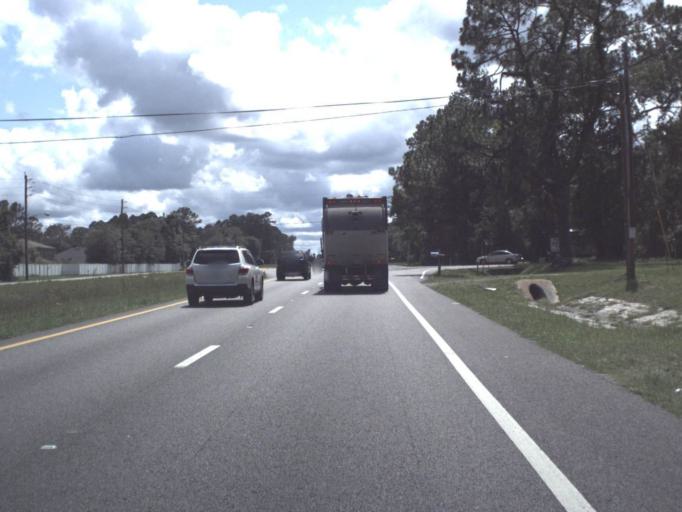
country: US
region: Florida
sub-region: Clay County
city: Bellair-Meadowbrook Terrace
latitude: 30.2733
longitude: -81.8362
